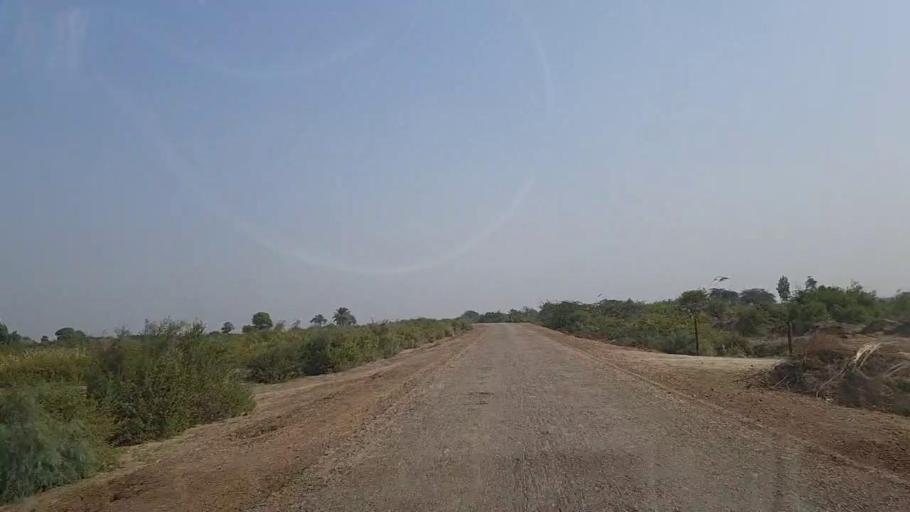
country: PK
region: Sindh
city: Keti Bandar
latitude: 24.2295
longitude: 67.6600
